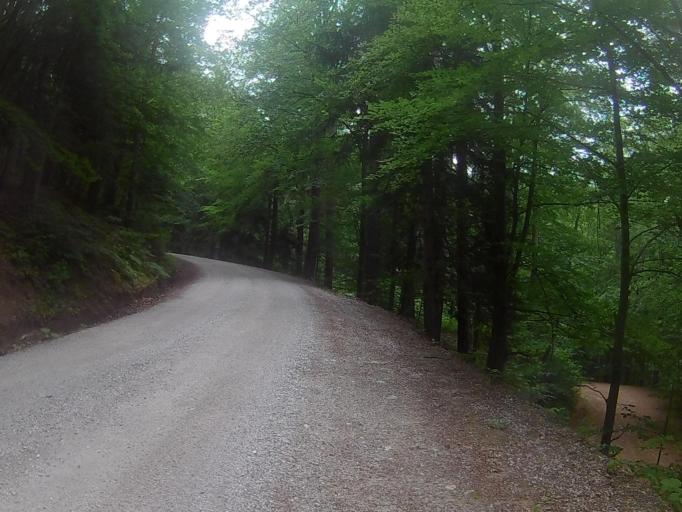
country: SI
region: Ruse
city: Ruse
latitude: 46.5255
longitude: 15.5364
